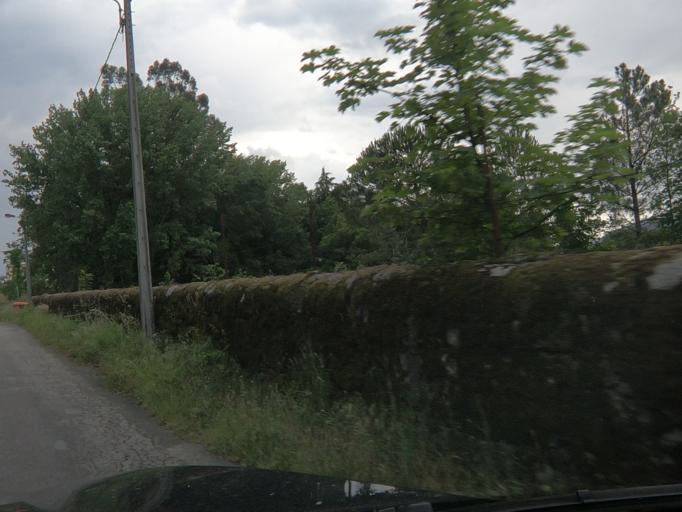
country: PT
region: Vila Real
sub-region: Vila Real
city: Vila Real
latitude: 41.3140
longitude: -7.7423
